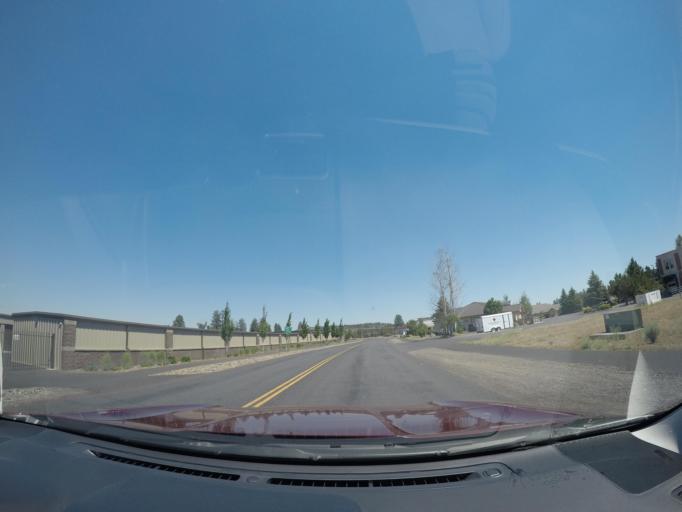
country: US
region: Oregon
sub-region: Deschutes County
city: Sisters
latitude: 44.2978
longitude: -121.5477
